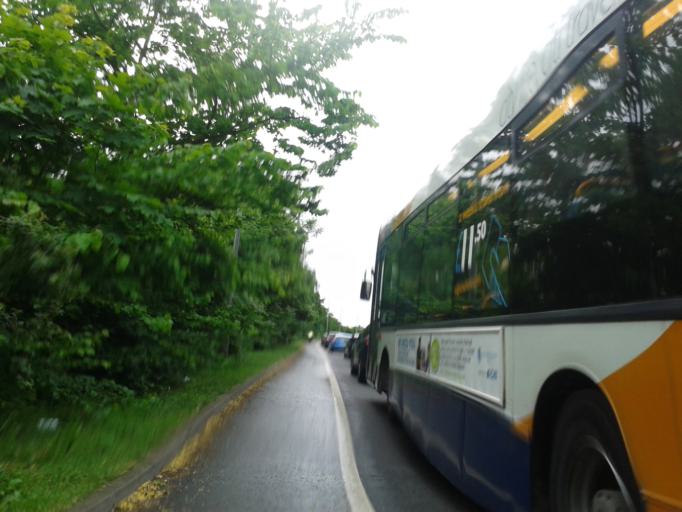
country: GB
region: England
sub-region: Cambridgeshire
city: Histon
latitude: 52.2434
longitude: 0.1122
